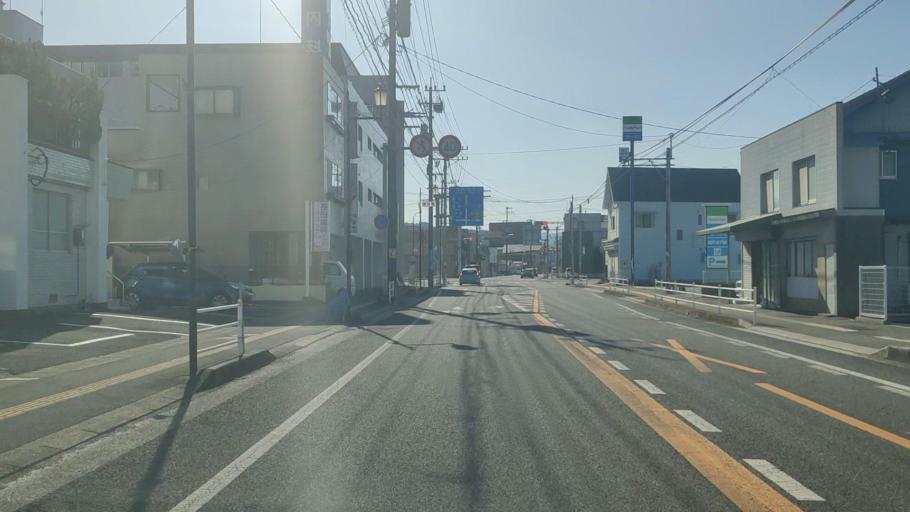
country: JP
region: Oita
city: Saiki
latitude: 32.9626
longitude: 131.8999
